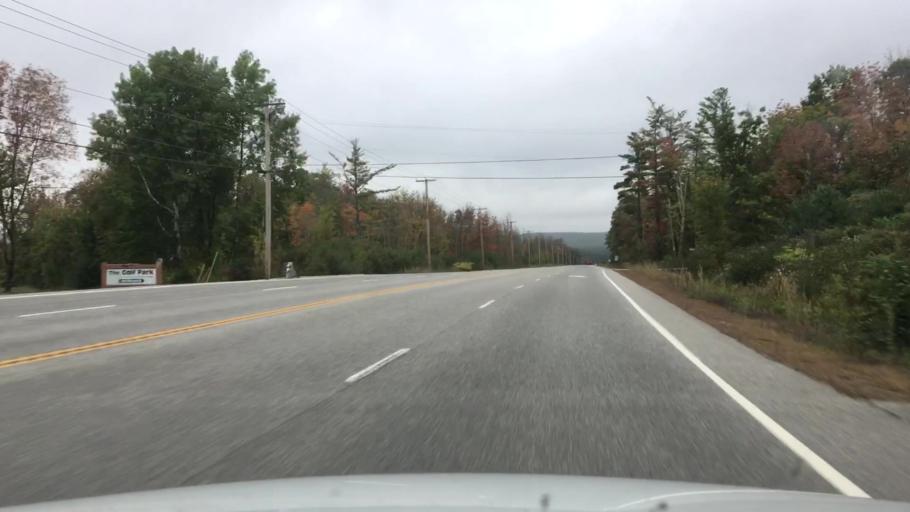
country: US
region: Maine
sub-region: Androscoggin County
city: Poland
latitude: 44.0258
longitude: -70.3662
